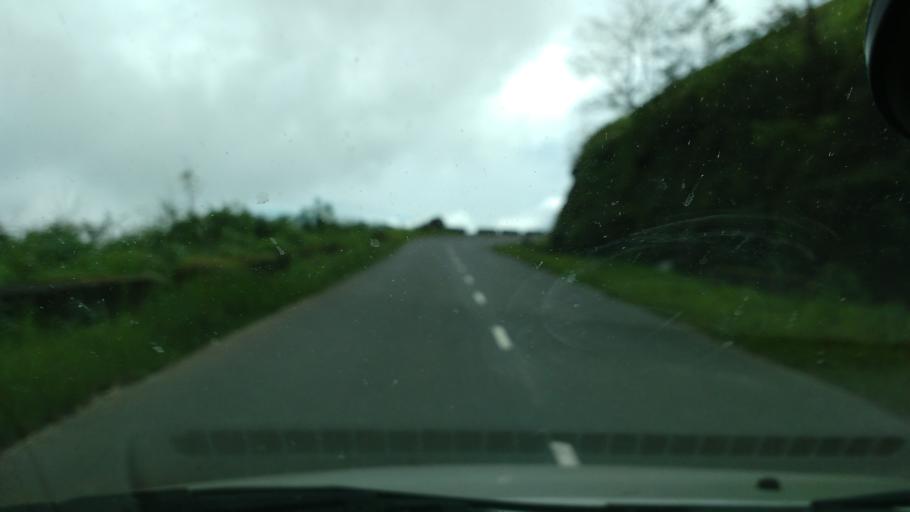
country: IN
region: Meghalaya
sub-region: East Khasi Hills
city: Shillong
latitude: 25.3879
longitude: 91.8731
